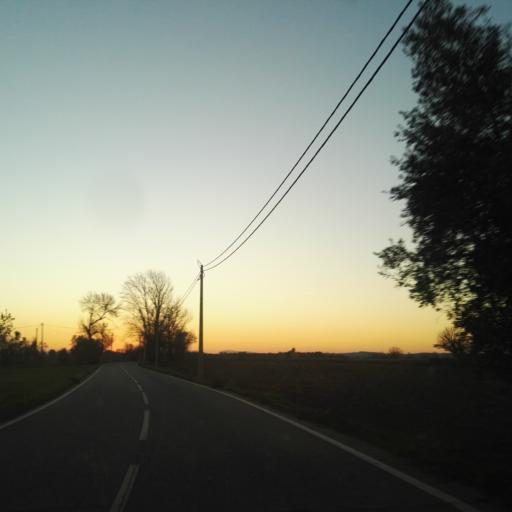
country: PT
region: Santarem
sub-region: Alpiarca
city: Alpiarca
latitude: 39.3028
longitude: -8.5466
